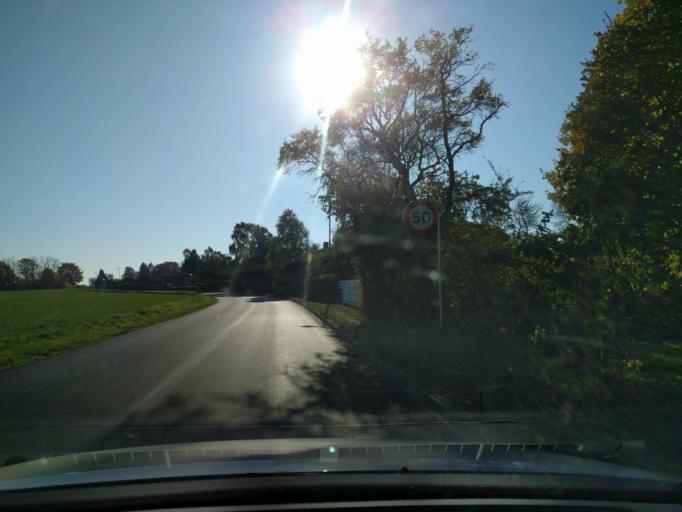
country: DK
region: Zealand
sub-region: Guldborgsund Kommune
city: Nykobing Falster
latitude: 54.8138
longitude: 11.8744
